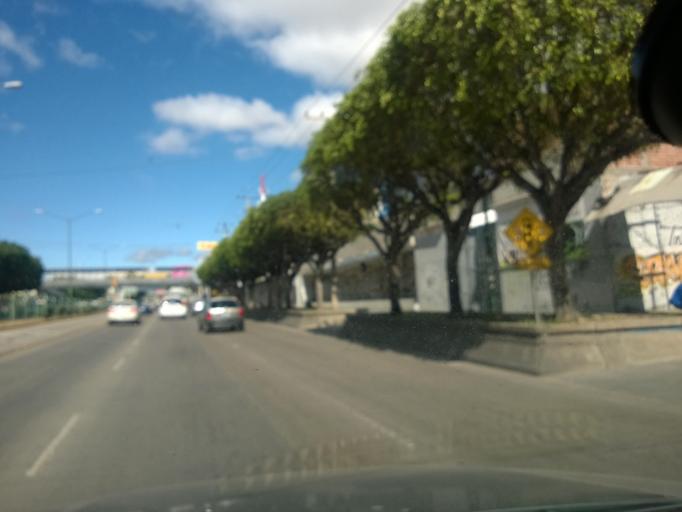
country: MX
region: Guanajuato
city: Leon
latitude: 21.1381
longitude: -101.6867
